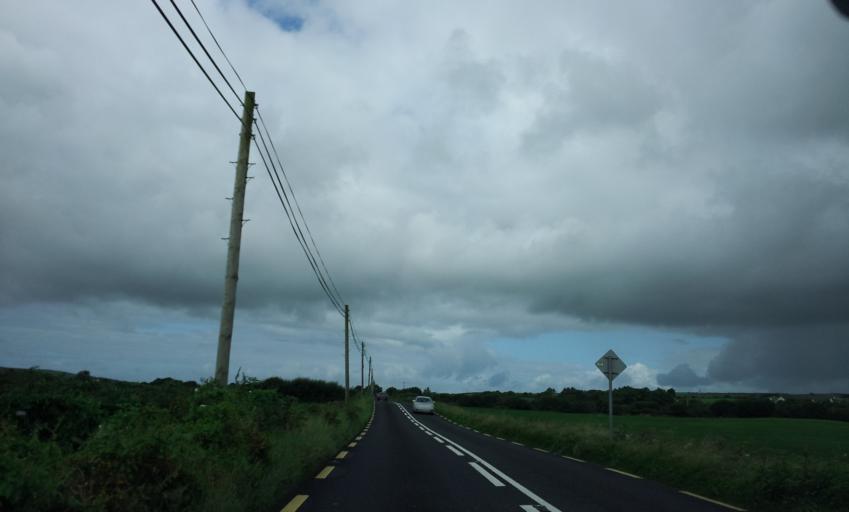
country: IE
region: Munster
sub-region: An Clar
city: Ennis
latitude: 52.9183
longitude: -9.2401
